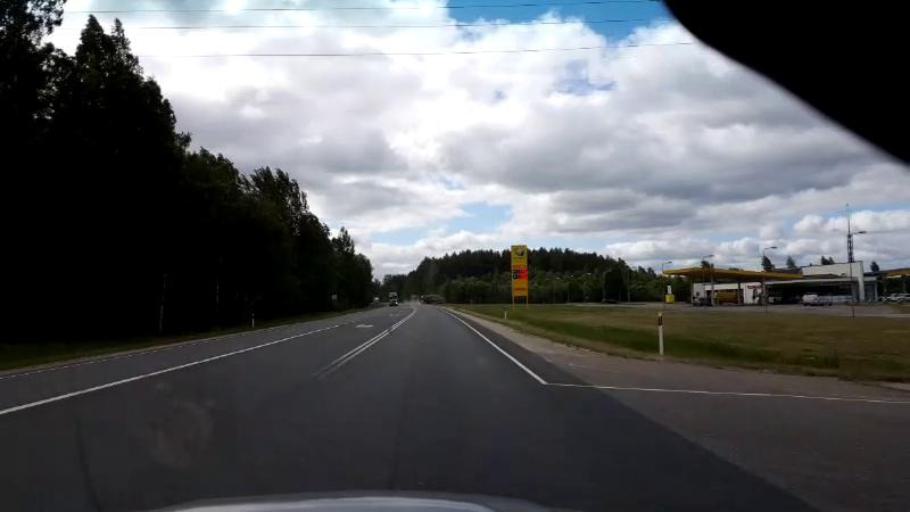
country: EE
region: Paernumaa
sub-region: Halinga vald
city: Parnu-Jaagupi
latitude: 58.7029
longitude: 24.4262
